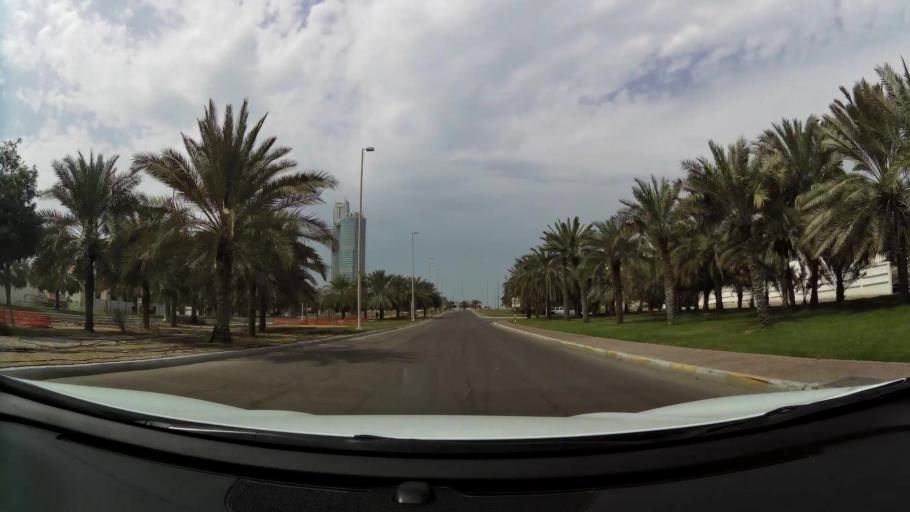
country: AE
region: Abu Dhabi
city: Abu Dhabi
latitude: 24.4613
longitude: 54.3371
